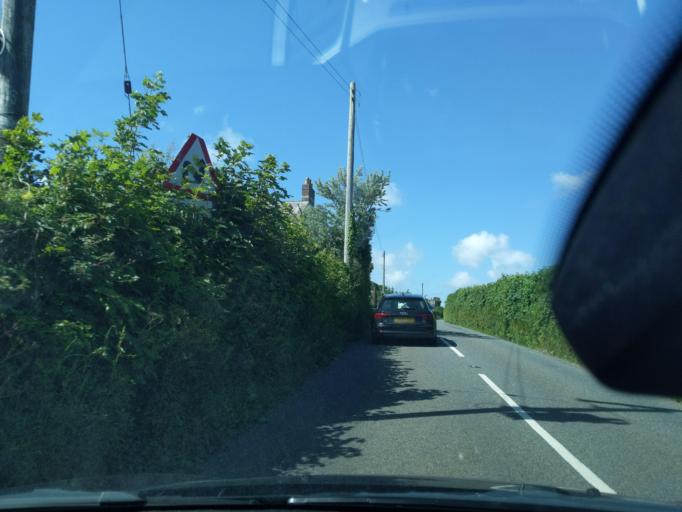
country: GB
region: England
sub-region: Devon
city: Fremington
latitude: 51.0345
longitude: -4.1003
